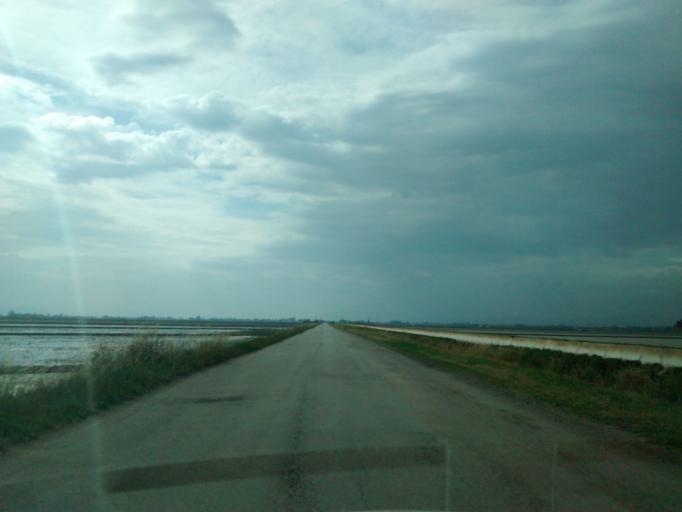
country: ES
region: Catalonia
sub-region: Provincia de Tarragona
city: Deltebre
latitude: 40.6940
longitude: 0.7686
